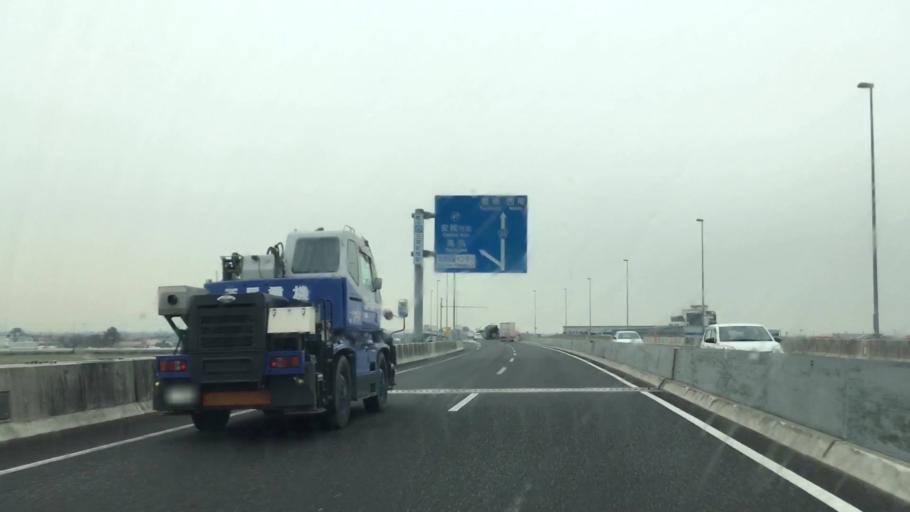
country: JP
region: Aichi
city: Anjo
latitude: 34.9513
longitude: 137.0376
